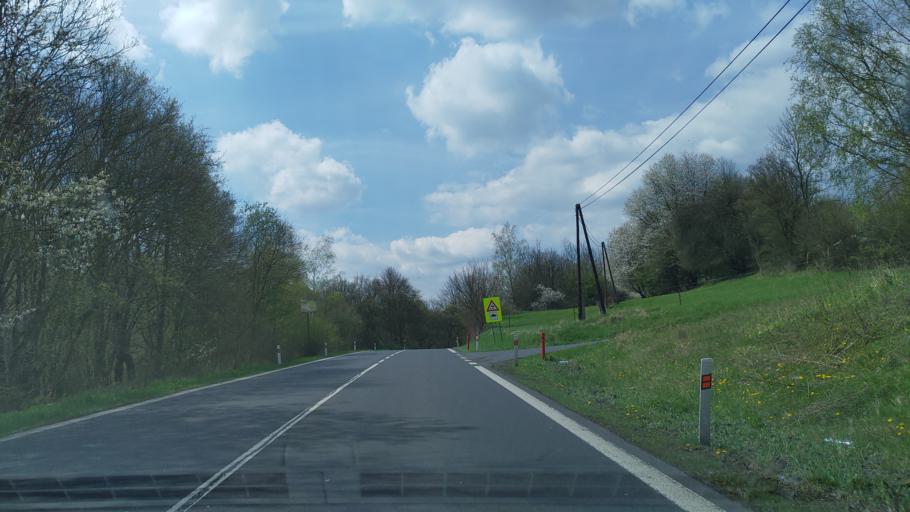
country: CZ
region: Ustecky
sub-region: Okres Chomutov
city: Perstejn
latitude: 50.3436
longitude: 13.0652
